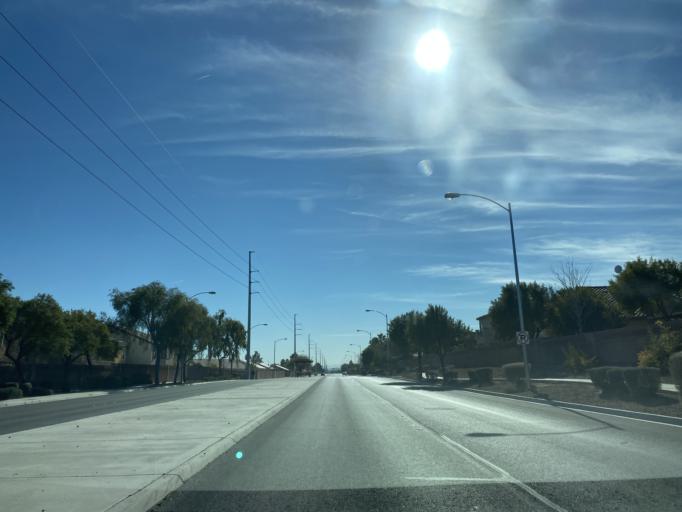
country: US
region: Nevada
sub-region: Clark County
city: North Las Vegas
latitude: 36.2606
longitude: -115.1440
